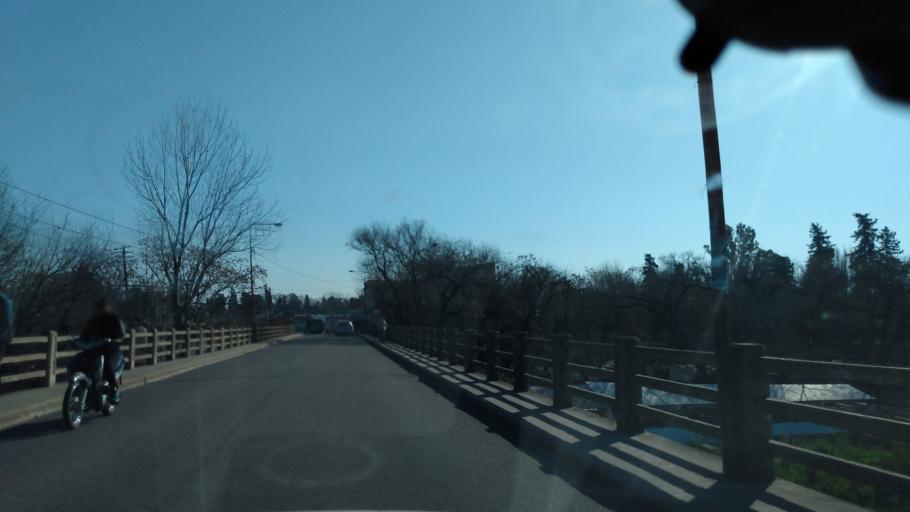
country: AR
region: Buenos Aires
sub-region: Partido de Lujan
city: Lujan
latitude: -34.5646
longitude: -59.1233
